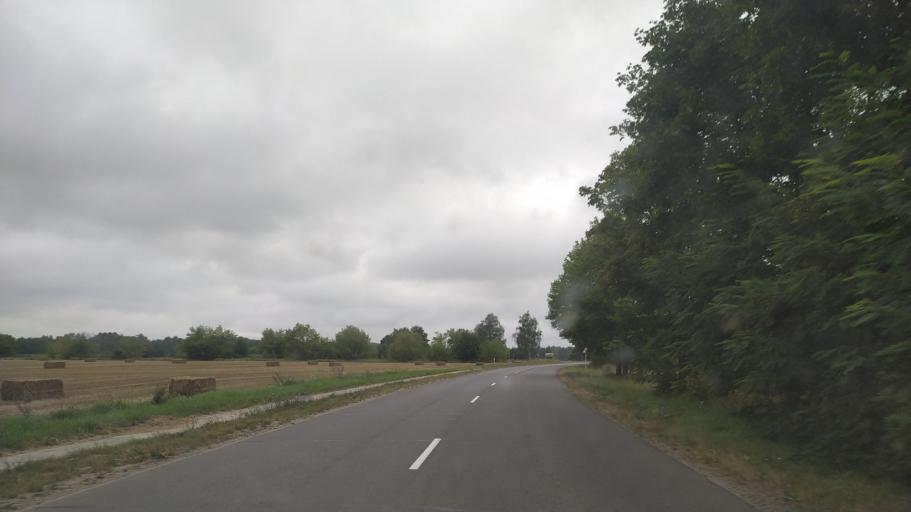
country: BY
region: Brest
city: Byaroza
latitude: 52.5563
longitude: 24.9178
